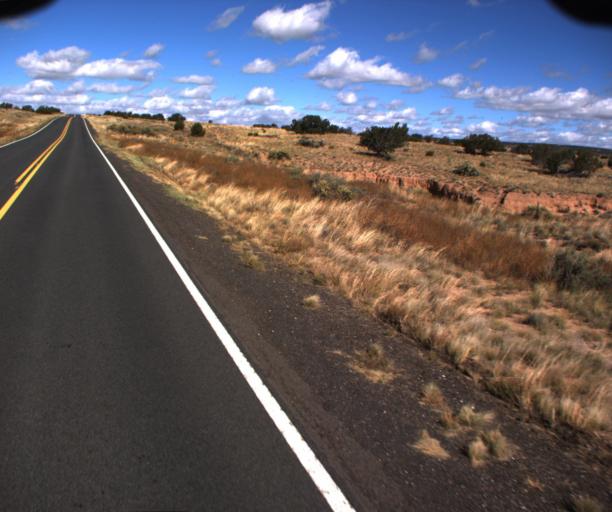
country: US
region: Arizona
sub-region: Apache County
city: Houck
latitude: 35.0176
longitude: -109.2392
